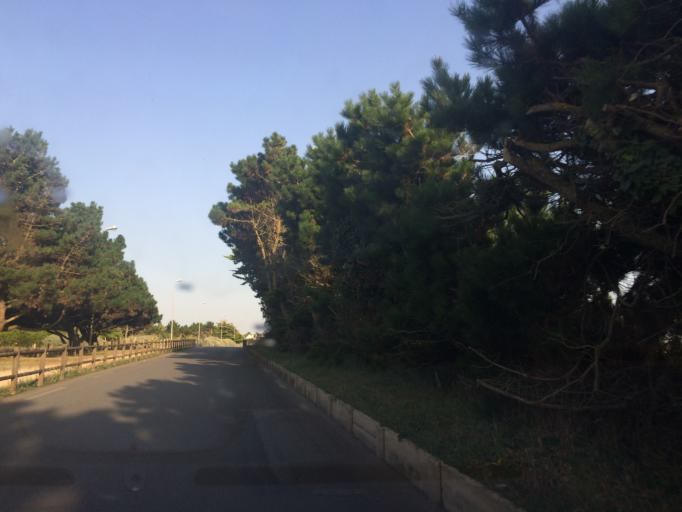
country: FR
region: Brittany
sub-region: Departement du Morbihan
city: Damgan
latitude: 47.5152
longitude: -2.5626
